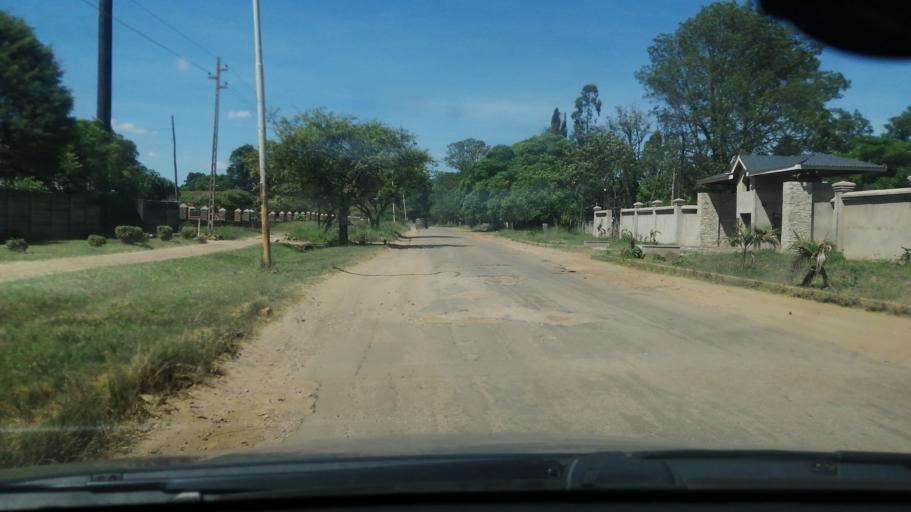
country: ZW
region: Harare
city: Epworth
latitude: -17.8213
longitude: 31.1279
